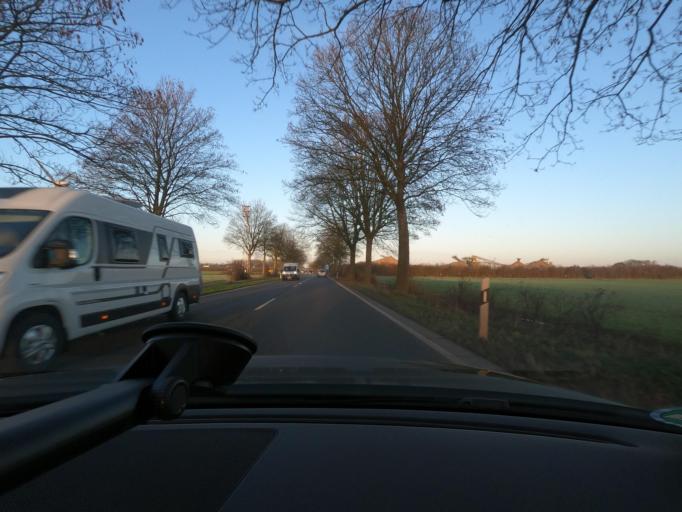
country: DE
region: North Rhine-Westphalia
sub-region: Regierungsbezirk Dusseldorf
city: Wachtendonk
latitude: 51.3937
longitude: 6.3714
